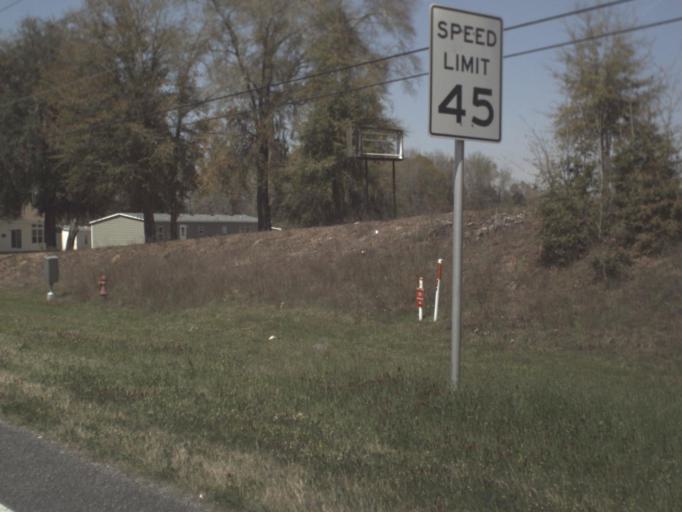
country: US
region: Florida
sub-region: Gadsden County
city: Midway
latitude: 30.4794
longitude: -84.4149
